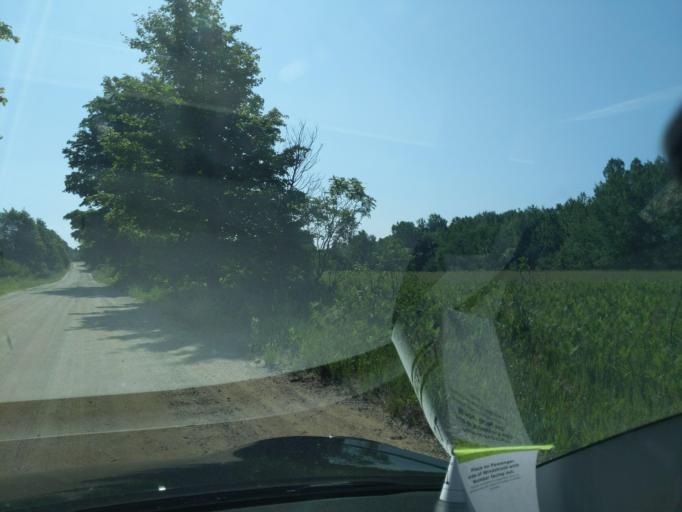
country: US
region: Michigan
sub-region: Mackinac County
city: Saint Ignace
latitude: 45.6981
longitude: -84.7237
